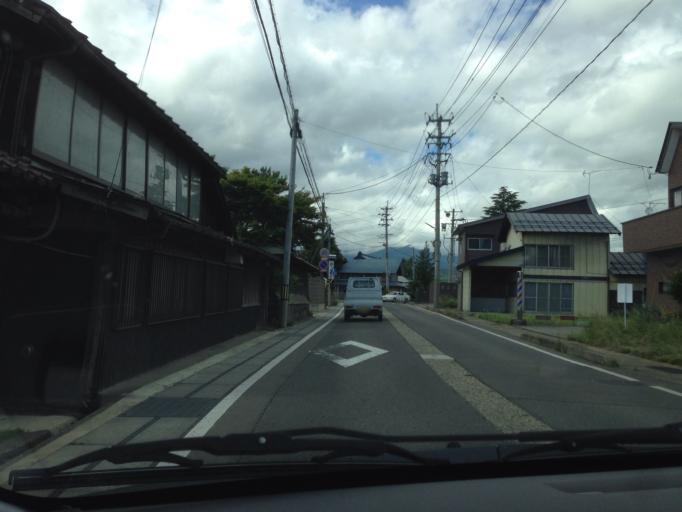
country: JP
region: Fukushima
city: Kitakata
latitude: 37.6748
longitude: 139.8716
